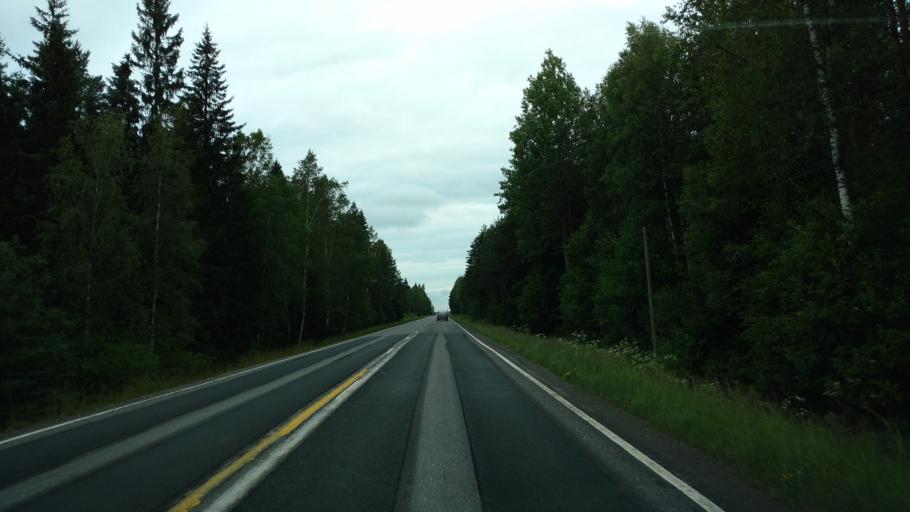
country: FI
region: Varsinais-Suomi
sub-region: Salo
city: Halikko
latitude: 60.4563
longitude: 23.0239
